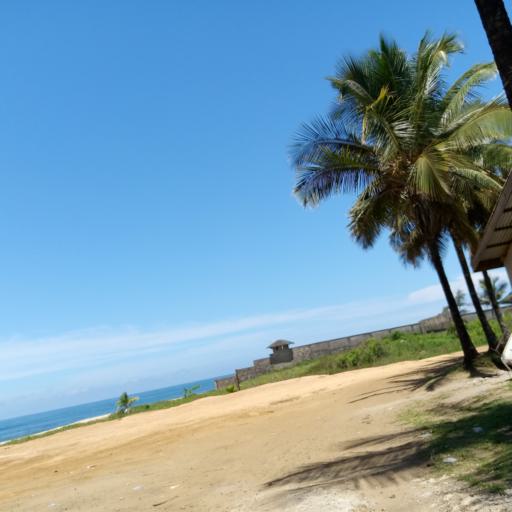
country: LR
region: Montserrado
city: Monrovia
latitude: 6.2354
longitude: -10.6950
